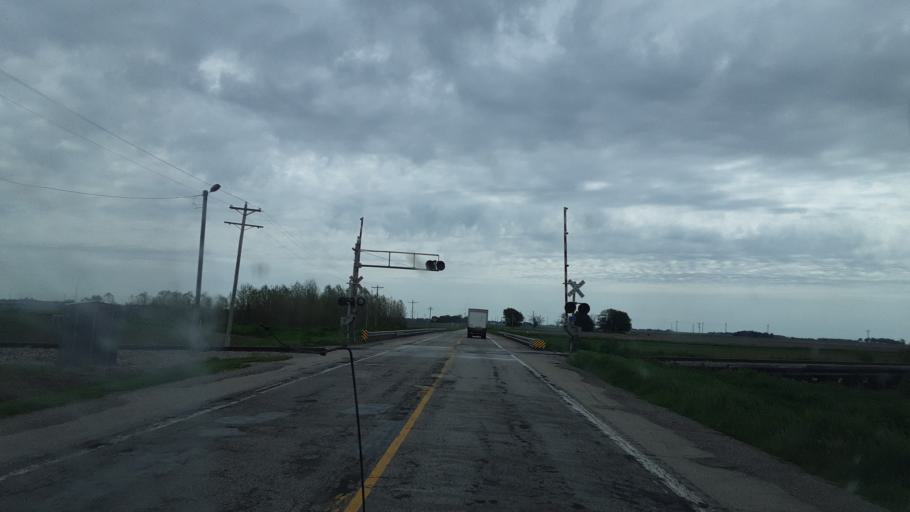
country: US
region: Illinois
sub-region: Tazewell County
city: Delavan
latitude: 40.3073
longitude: -89.4928
